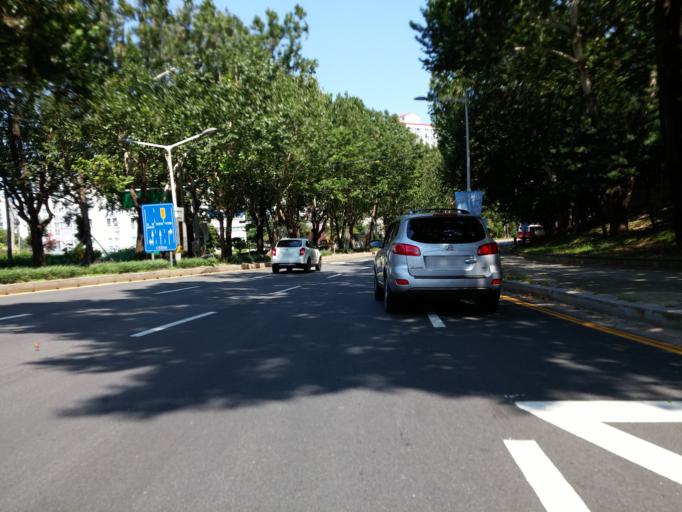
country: KR
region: Chungcheongbuk-do
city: Cheongju-si
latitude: 36.6323
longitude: 127.4320
